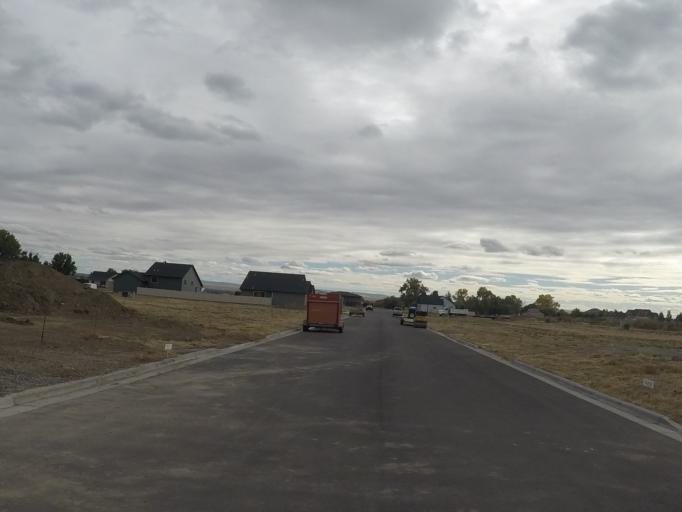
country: US
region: Montana
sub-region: Yellowstone County
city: Laurel
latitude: 45.7798
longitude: -108.6618
